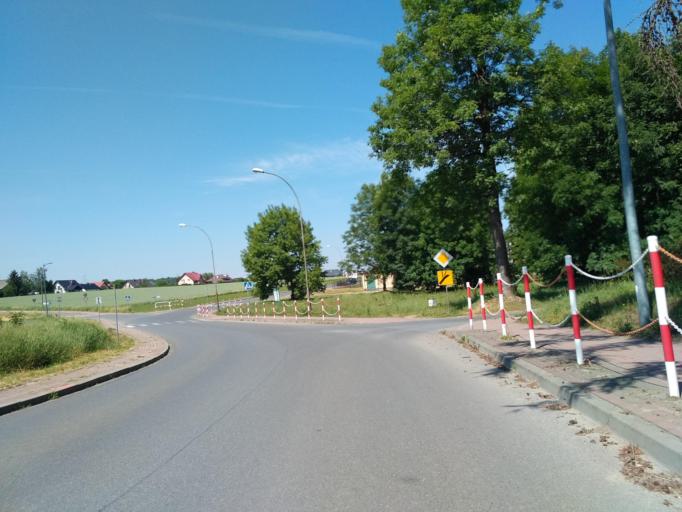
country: PL
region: Subcarpathian Voivodeship
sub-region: Powiat krosnienski
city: Korczyna
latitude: 49.7114
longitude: 21.8073
